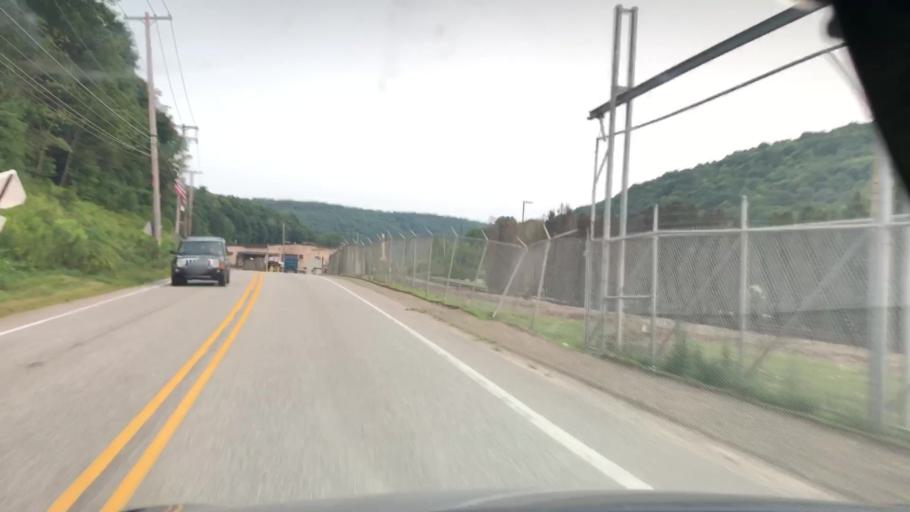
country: US
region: Pennsylvania
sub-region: Venango County
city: Hasson Heights
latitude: 41.4674
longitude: -79.6912
